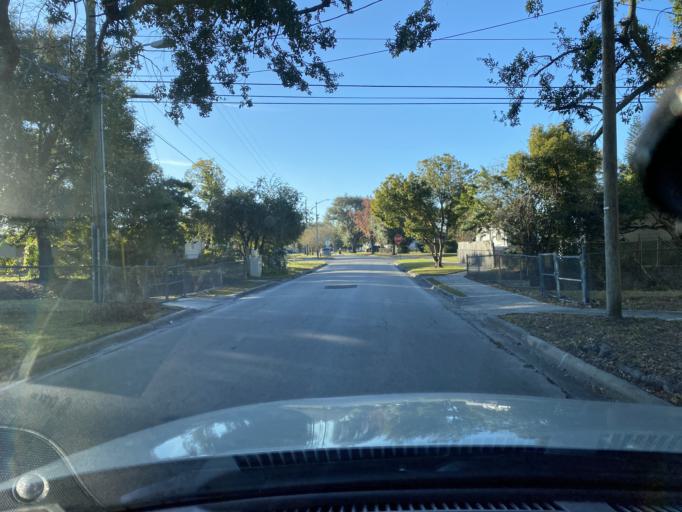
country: US
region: Florida
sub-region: Orange County
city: Azalea Park
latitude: 28.5321
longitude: -81.2966
